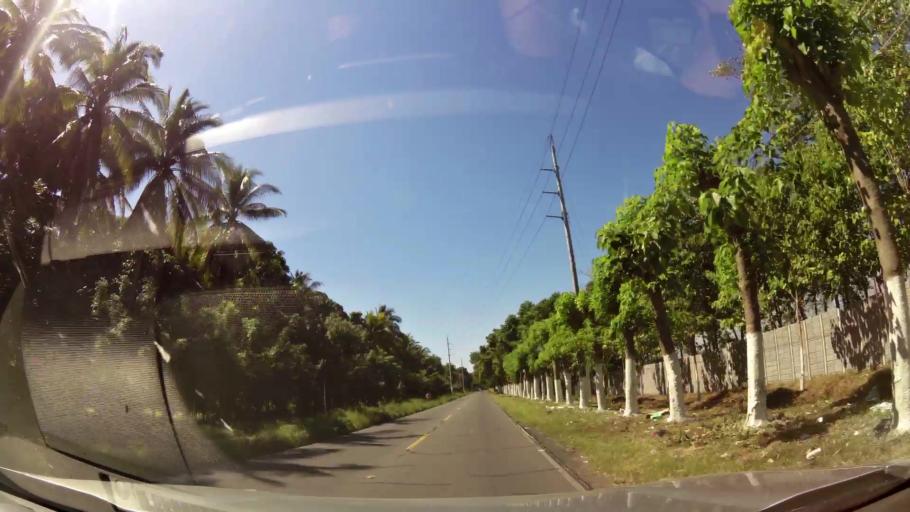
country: GT
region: Escuintla
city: Iztapa
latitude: 13.9368
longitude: -90.7301
